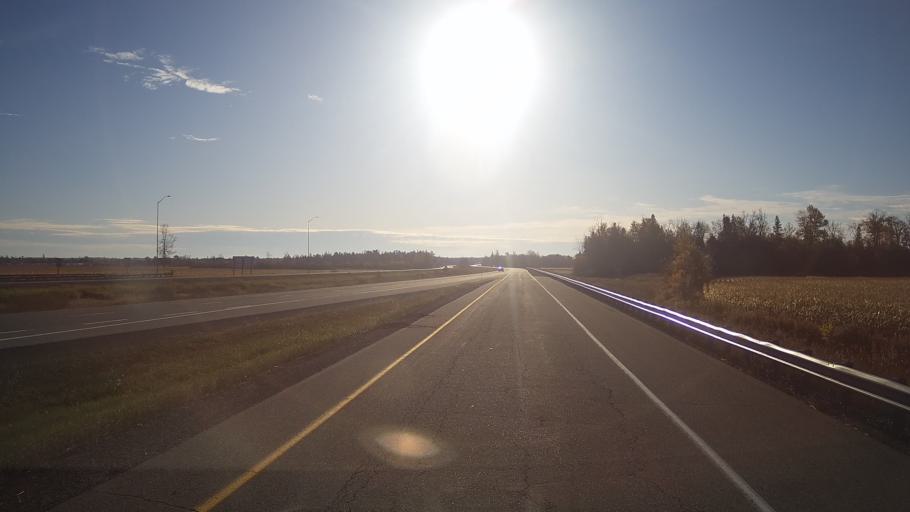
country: CA
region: Ontario
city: Arnprior
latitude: 45.3607
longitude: -76.2323
